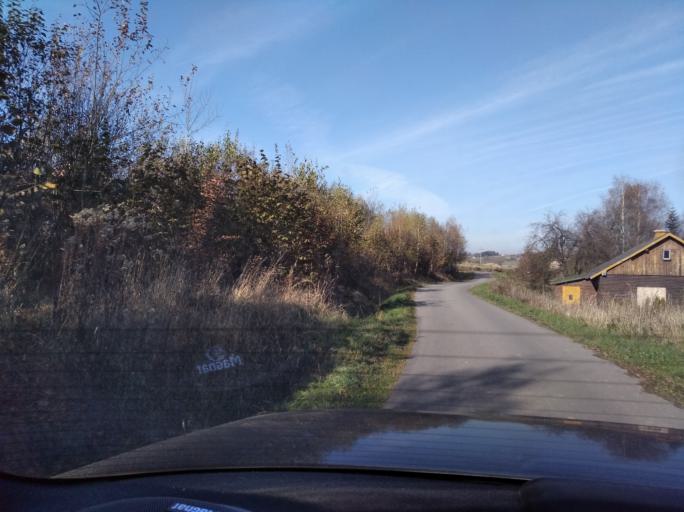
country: PL
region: Subcarpathian Voivodeship
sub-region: Powiat ropczycko-sedziszowski
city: Wielopole Skrzynskie
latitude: 49.9237
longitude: 21.5585
